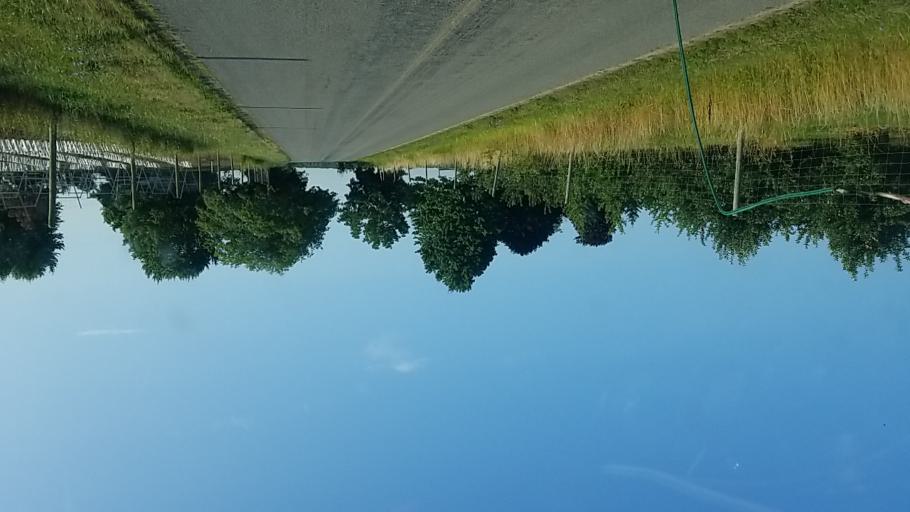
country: US
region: Michigan
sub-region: Newaygo County
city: Newaygo
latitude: 43.3588
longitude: -85.8208
